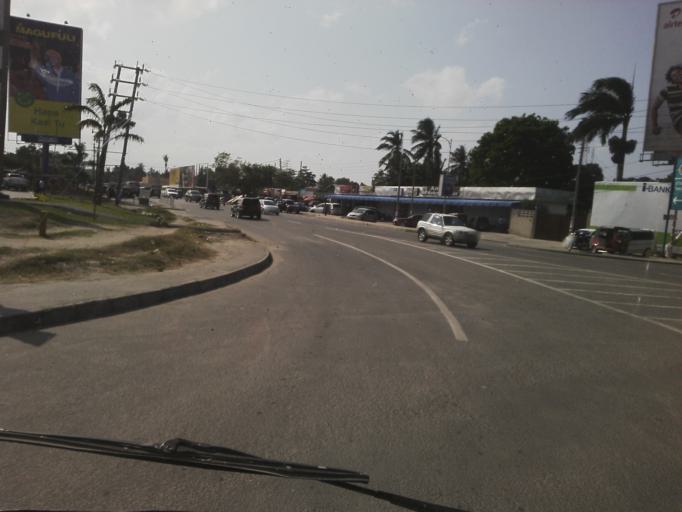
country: TZ
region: Dar es Salaam
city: Magomeni
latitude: -6.7725
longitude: 39.2221
